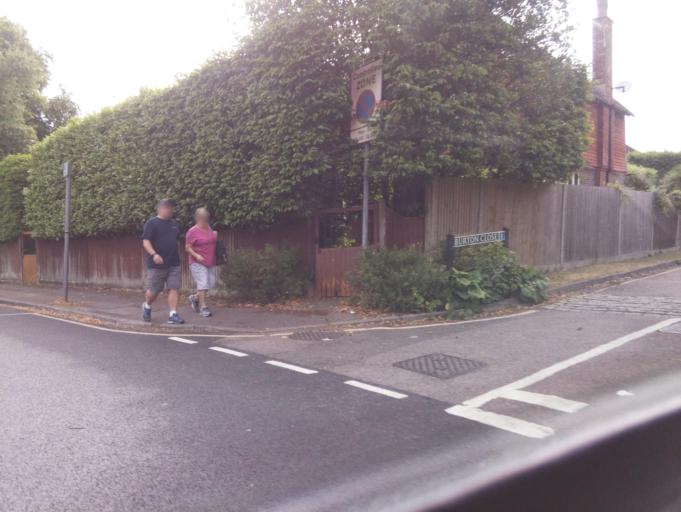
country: GB
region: England
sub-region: Surrey
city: Horley
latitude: 51.1694
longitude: -0.1646
